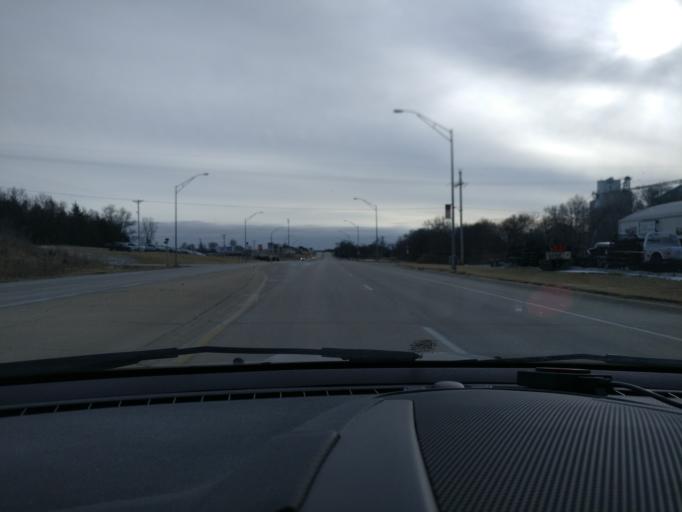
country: US
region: Nebraska
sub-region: Saunders County
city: Wahoo
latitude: 41.0607
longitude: -96.6403
